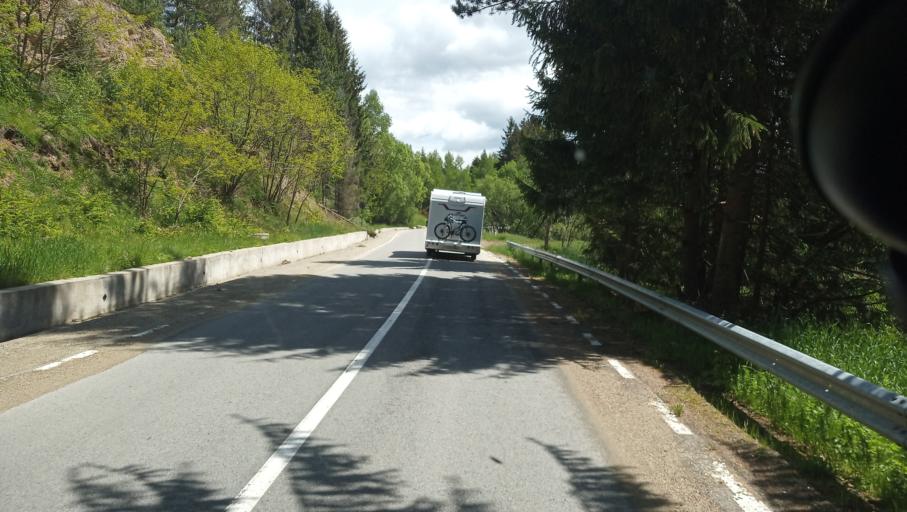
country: RO
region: Caras-Severin
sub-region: Comuna Brebu Nou
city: Brebu Nou
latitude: 45.2170
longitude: 22.0930
